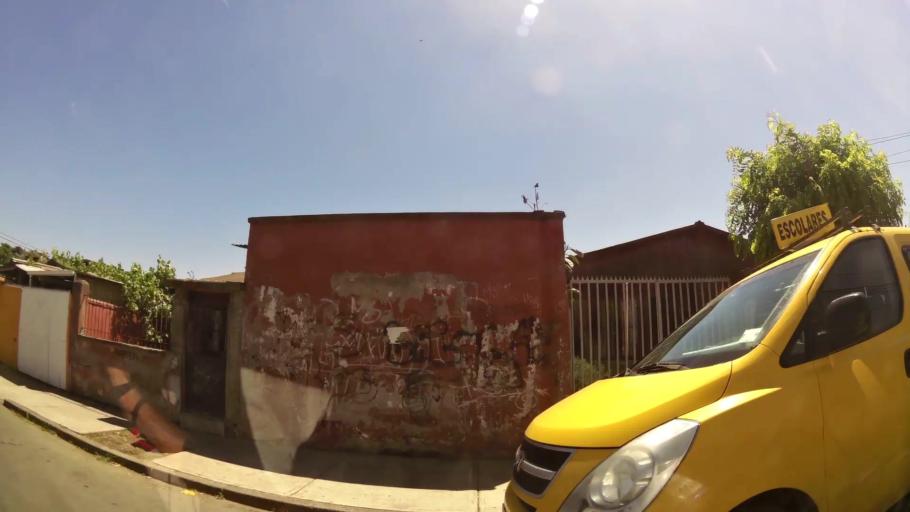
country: CL
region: Santiago Metropolitan
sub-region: Provincia de Maipo
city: San Bernardo
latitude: -33.5669
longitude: -70.6823
